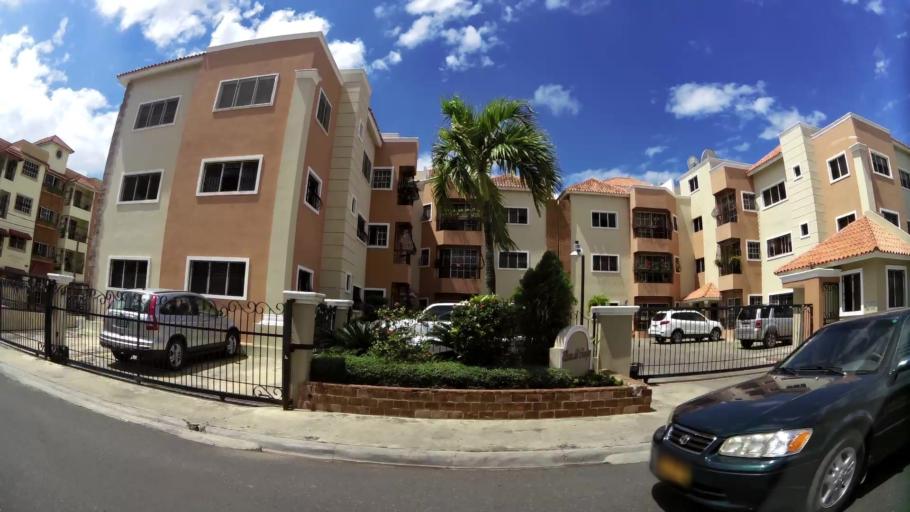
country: DO
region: Santiago
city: Santiago de los Caballeros
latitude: 19.4578
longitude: -70.6619
